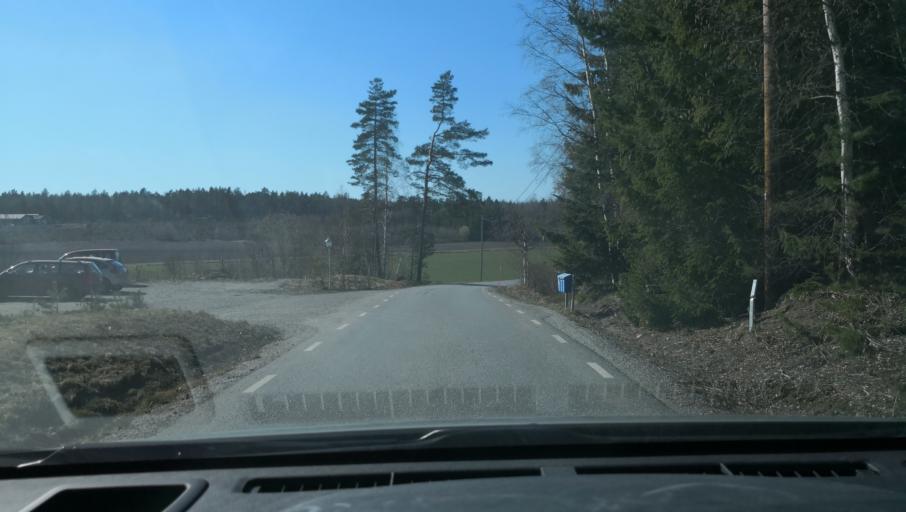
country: SE
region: Vaestmanland
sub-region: Sala Kommun
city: Sala
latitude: 59.9275
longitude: 16.4671
